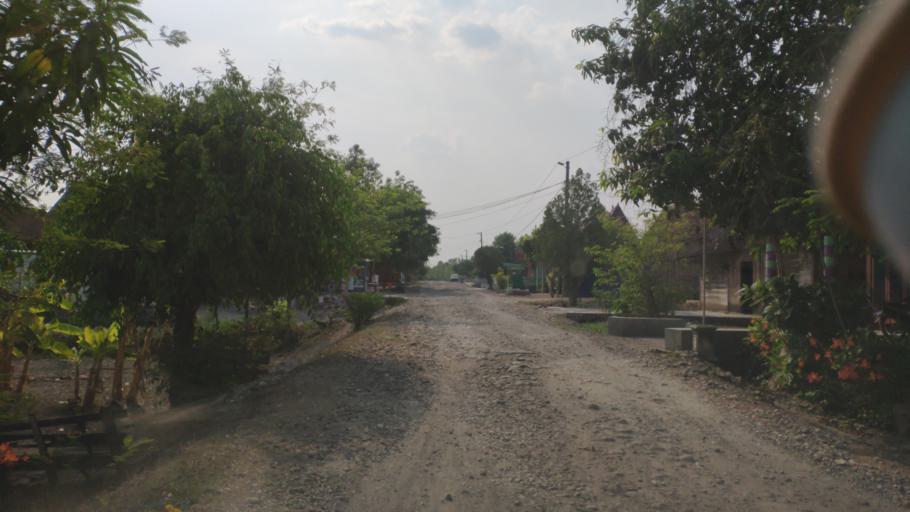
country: ID
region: Central Java
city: Randublatung
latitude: -7.2828
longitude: 111.2539
